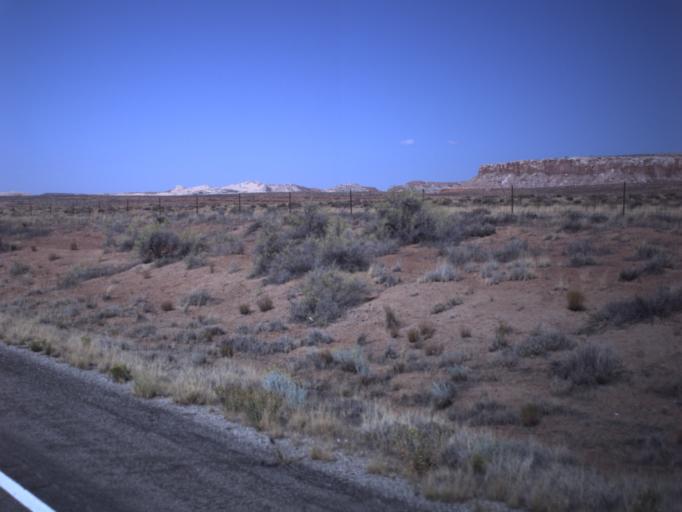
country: US
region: Utah
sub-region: San Juan County
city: Blanding
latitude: 37.2681
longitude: -109.6052
